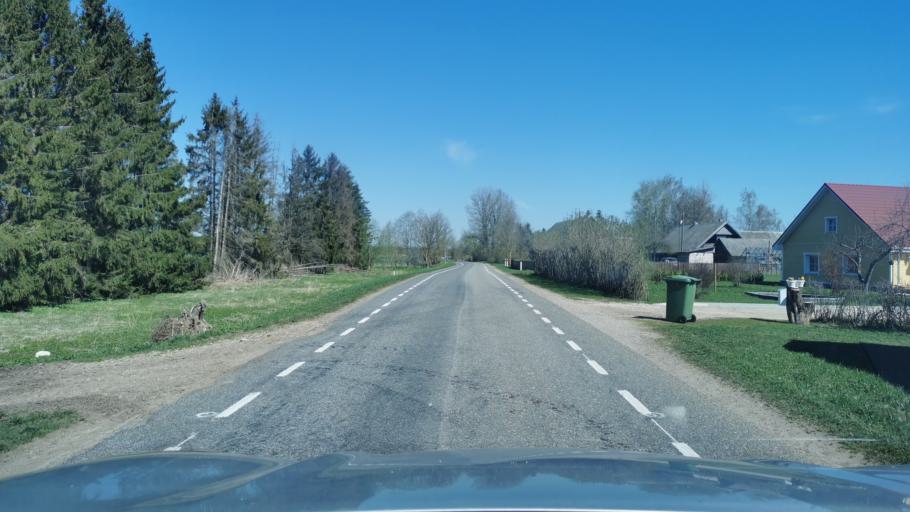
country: EE
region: Laeaene-Virumaa
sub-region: Vinni vald
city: Vinni
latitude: 59.0963
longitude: 26.6164
